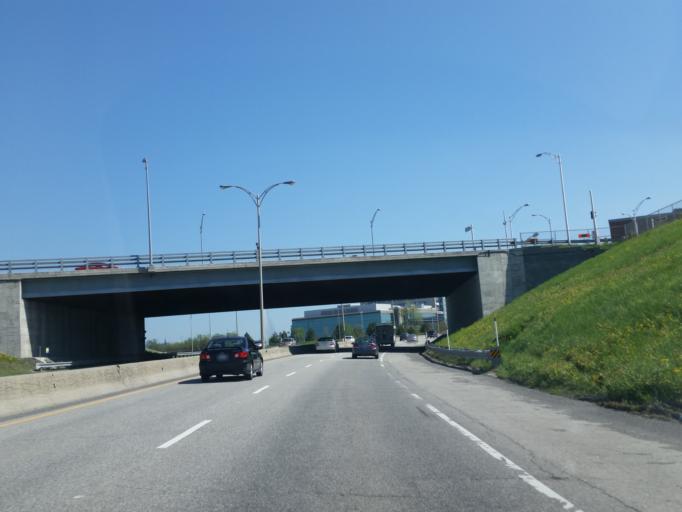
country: CA
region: Quebec
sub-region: Outaouais
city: Gatineau
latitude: 45.4491
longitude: -75.7326
